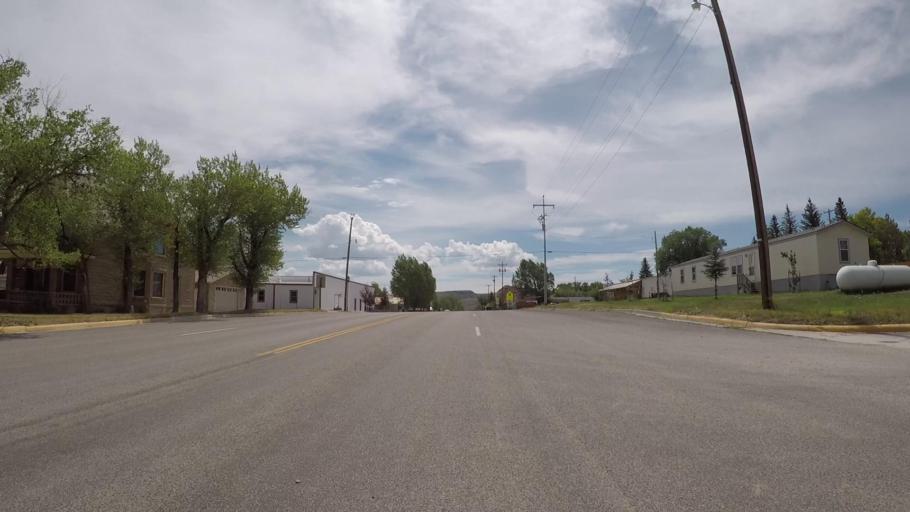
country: US
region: Wyoming
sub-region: Carbon County
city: Saratoga
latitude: 41.2079
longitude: -106.7950
